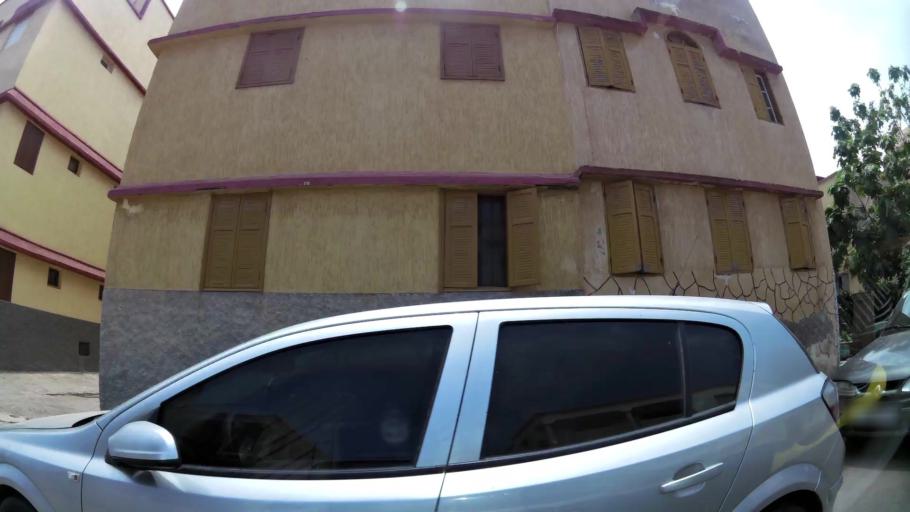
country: MA
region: Rabat-Sale-Zemmour-Zaer
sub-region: Rabat
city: Rabat
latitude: 33.9874
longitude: -6.8871
